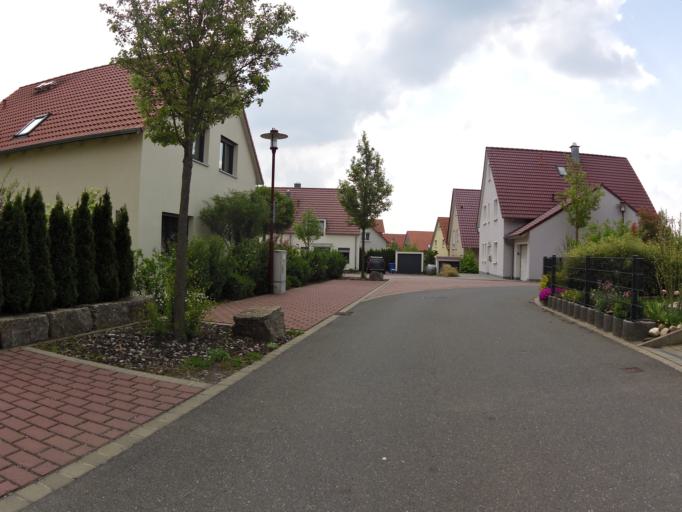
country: DE
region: Bavaria
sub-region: Regierungsbezirk Unterfranken
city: Kurnach
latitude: 49.8513
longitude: 10.0497
